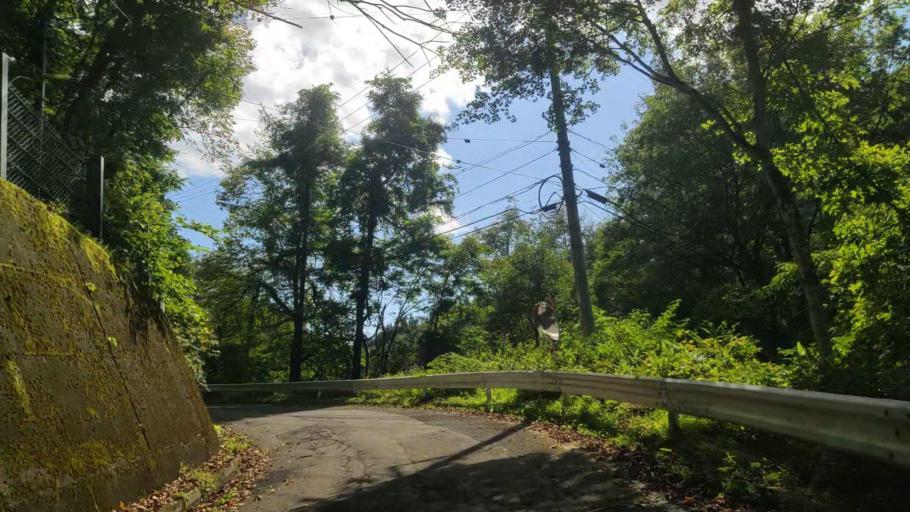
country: JP
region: Gunma
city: Nakanojomachi
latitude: 36.6617
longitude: 138.6214
